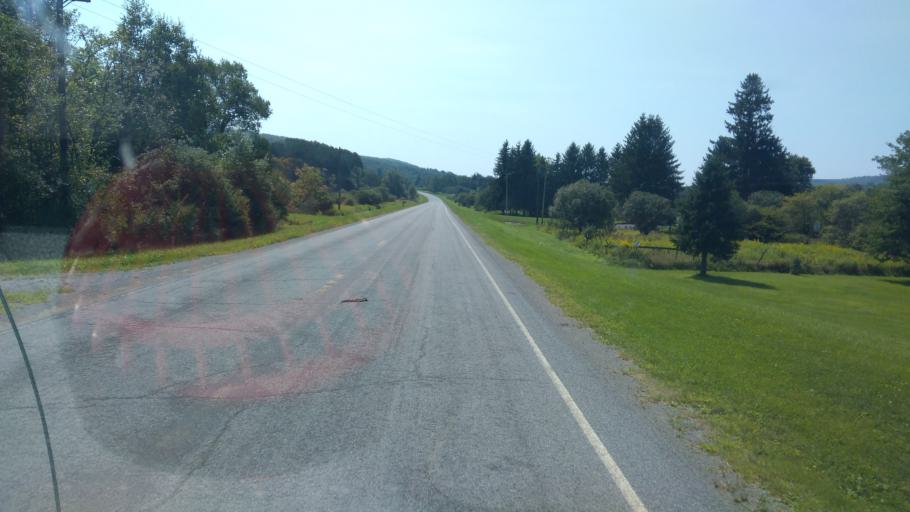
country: US
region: New York
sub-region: Allegany County
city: Belmont
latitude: 42.3389
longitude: -77.9302
